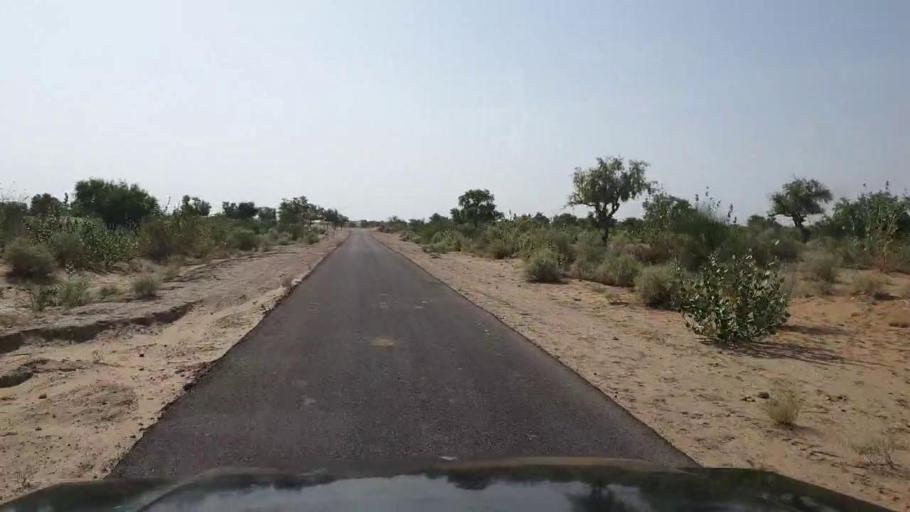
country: PK
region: Sindh
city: Islamkot
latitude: 24.9412
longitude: 70.0761
